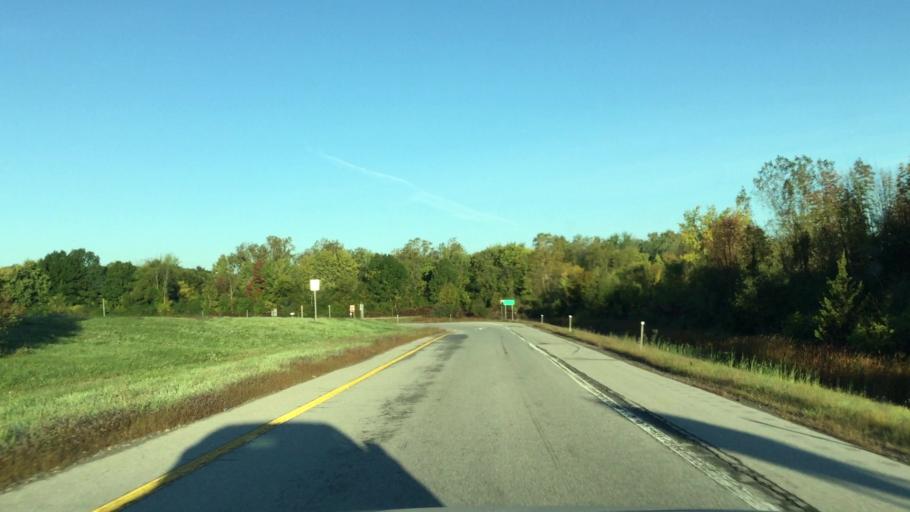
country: US
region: Michigan
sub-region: Genesee County
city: Beecher
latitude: 43.0980
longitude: -83.7312
